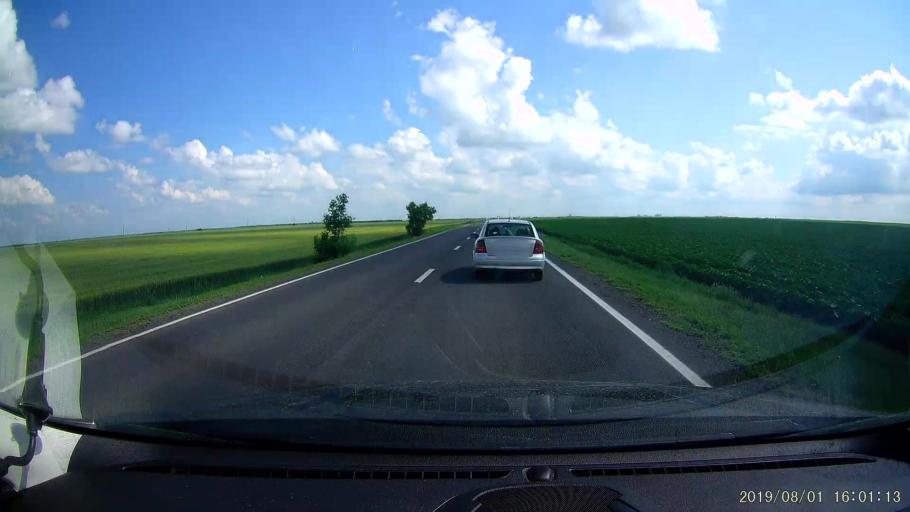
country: RO
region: Ialomita
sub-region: Comuna Ciulnita
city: Ciulnita
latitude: 44.5125
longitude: 27.3901
